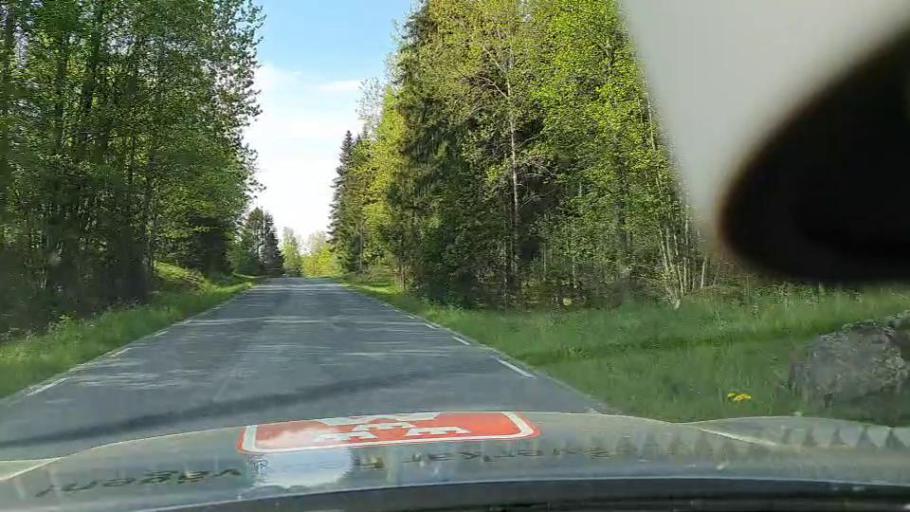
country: SE
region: Soedermanland
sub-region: Eskilstuna Kommun
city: Arla
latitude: 59.2627
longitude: 16.6548
